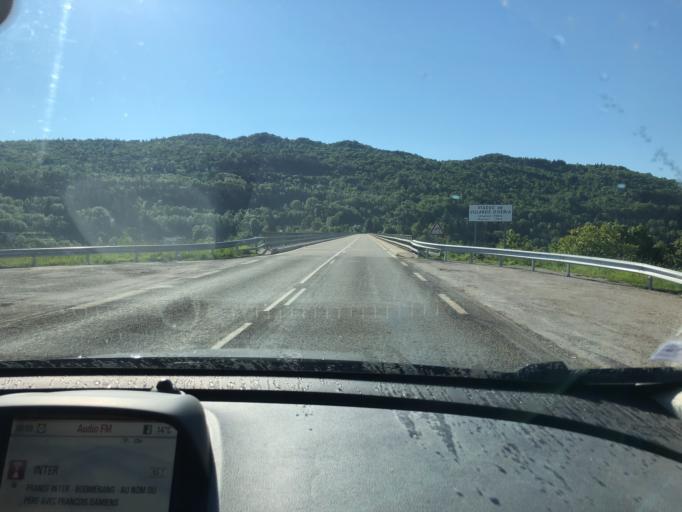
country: FR
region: Franche-Comte
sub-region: Departement du Jura
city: Moirans-en-Montagne
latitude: 46.4123
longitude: 5.7268
